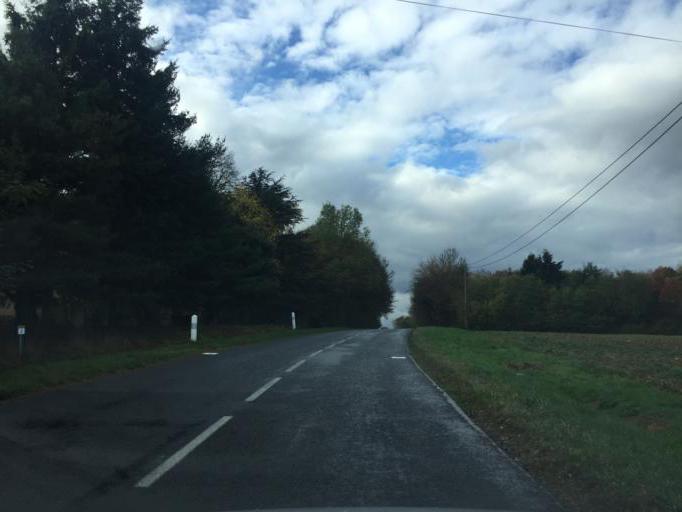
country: FR
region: Rhone-Alpes
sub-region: Departement de l'Ain
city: Mionnay
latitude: 45.9129
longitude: 4.9161
